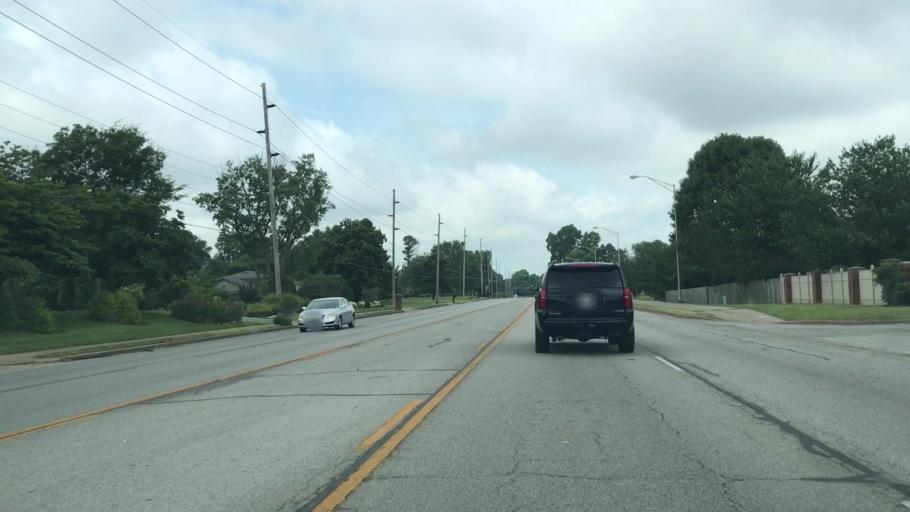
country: US
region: Kentucky
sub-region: Warren County
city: Bowling Green
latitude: 36.9896
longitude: -86.4121
